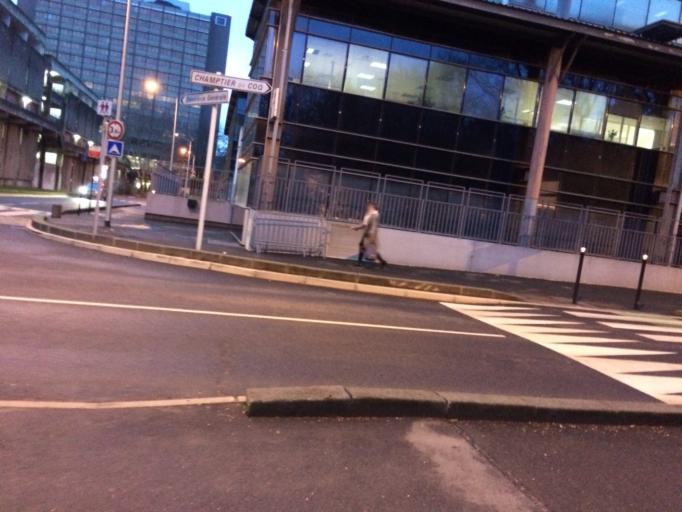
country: FR
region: Ile-de-France
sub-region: Departement de l'Essonne
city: Evry
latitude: 48.6260
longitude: 2.4340
